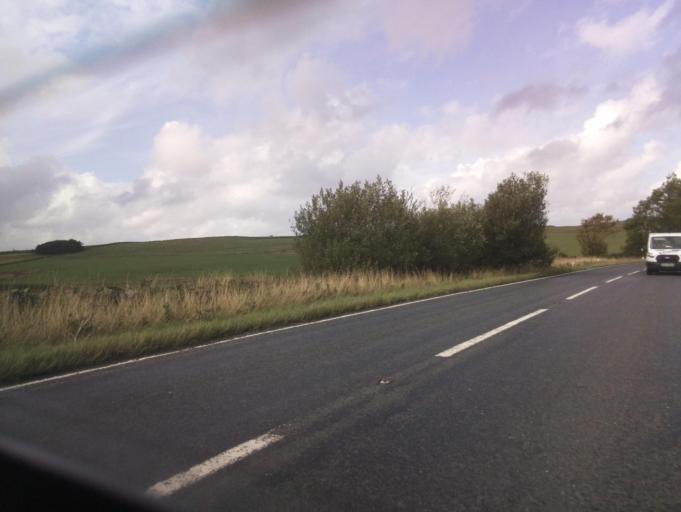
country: GB
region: England
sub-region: County Durham
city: Castleside
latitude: 54.7848
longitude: -1.8564
